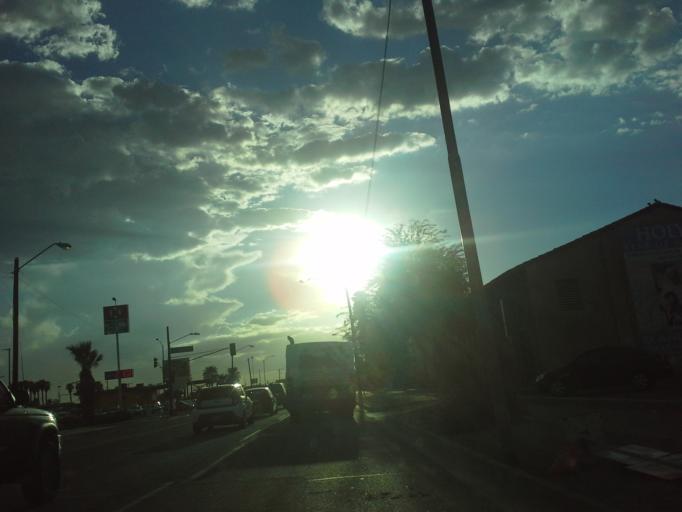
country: US
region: Arizona
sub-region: Maricopa County
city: Phoenix
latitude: 33.4513
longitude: -112.1035
